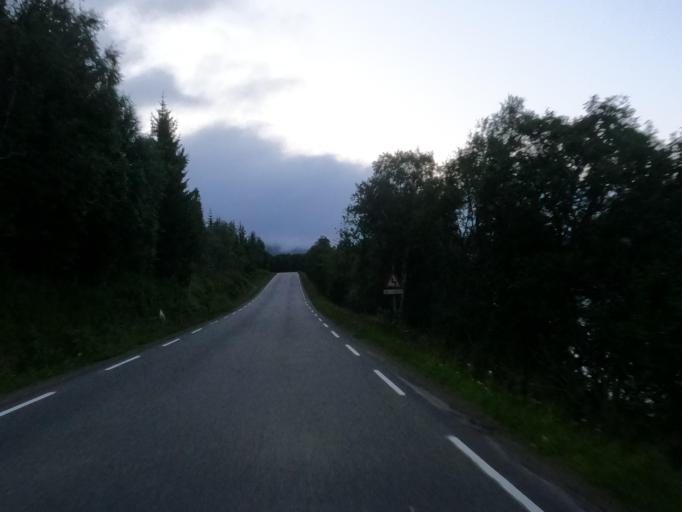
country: NO
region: Nordland
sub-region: Lodingen
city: Lodingen
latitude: 68.5966
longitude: 15.7884
